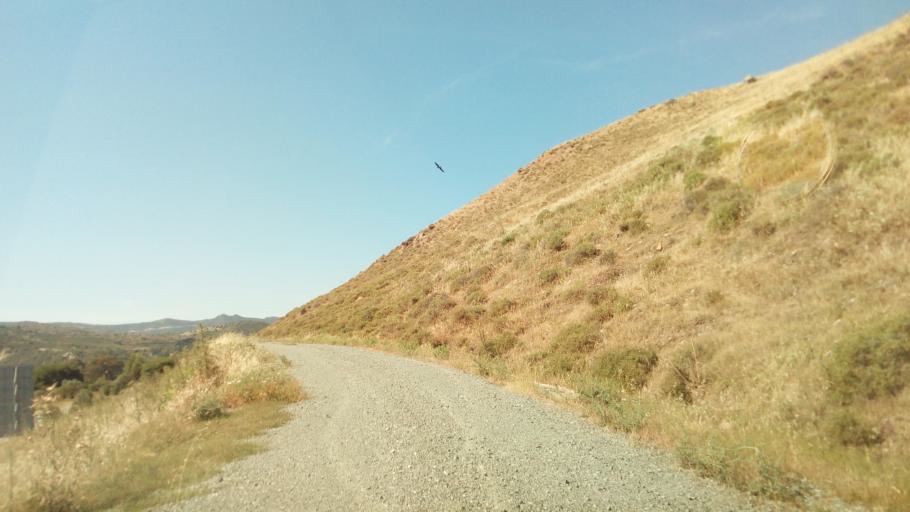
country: CY
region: Limassol
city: Pachna
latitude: 34.8124
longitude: 32.7143
